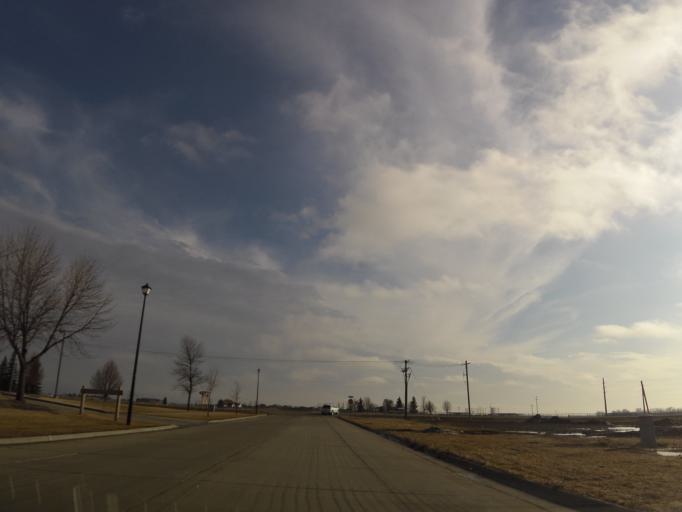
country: US
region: North Dakota
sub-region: Grand Forks County
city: Grand Forks
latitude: 47.8758
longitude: -97.0643
